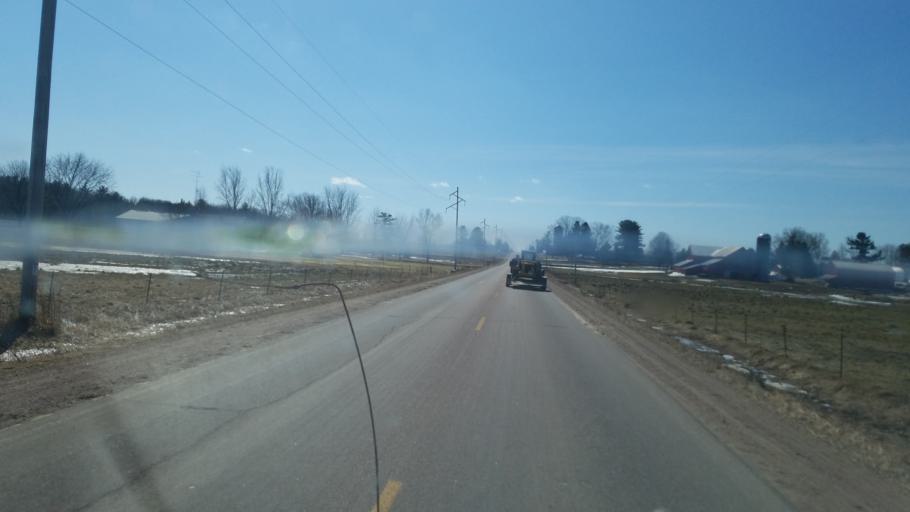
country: US
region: Wisconsin
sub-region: Clark County
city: Loyal
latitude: 44.5714
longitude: -90.3958
